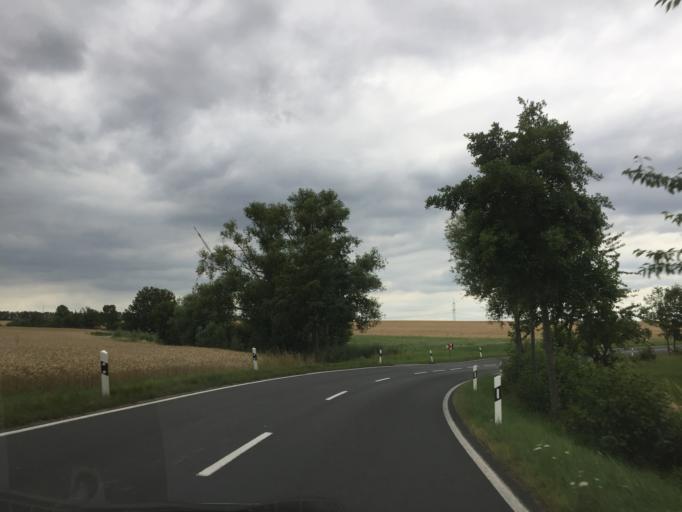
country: DE
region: Thuringia
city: Schmolln
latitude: 50.8751
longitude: 12.3803
